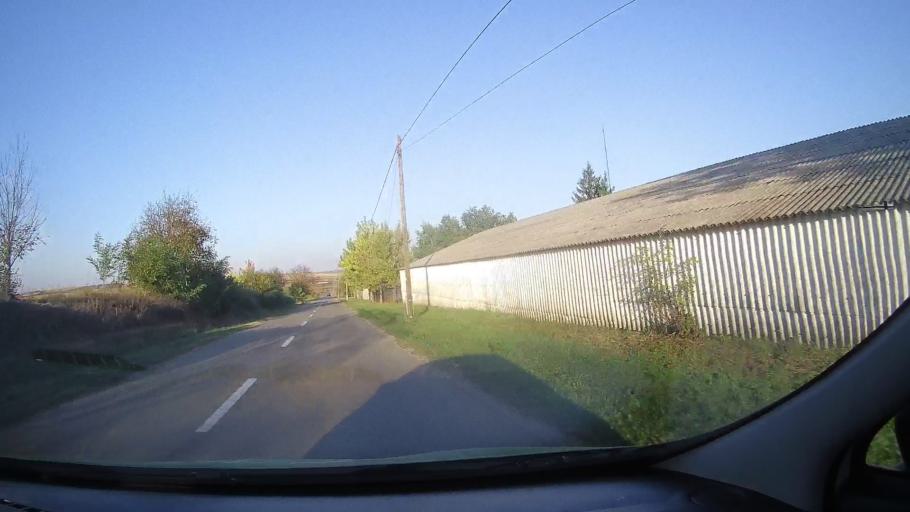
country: RO
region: Bihor
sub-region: Comuna Paleu
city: Paleu
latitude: 47.1172
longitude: 21.9481
